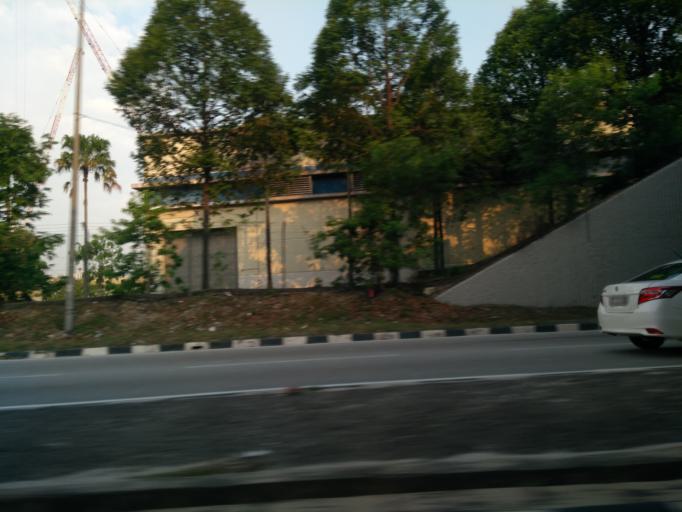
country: MY
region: Kuala Lumpur
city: Kuala Lumpur
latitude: 3.1167
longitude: 101.7074
